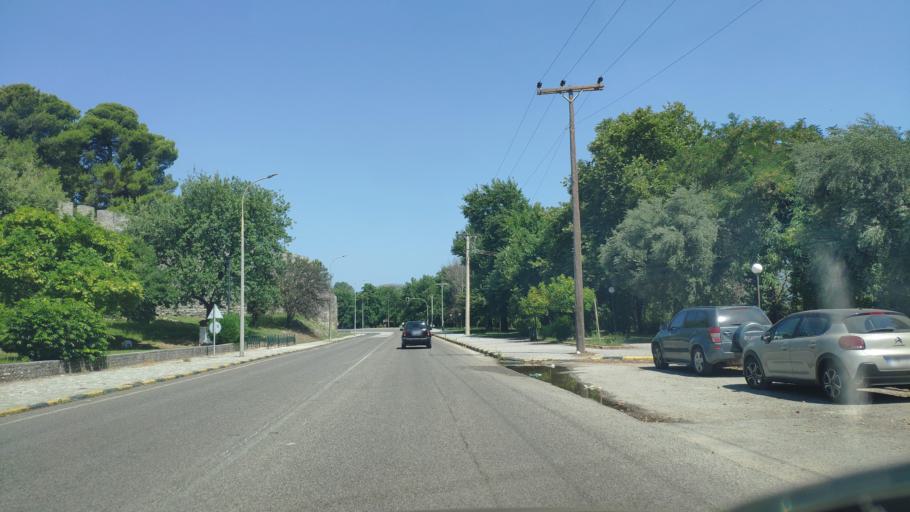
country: GR
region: Epirus
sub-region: Nomos Artas
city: Arta
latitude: 39.1654
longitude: 20.9899
